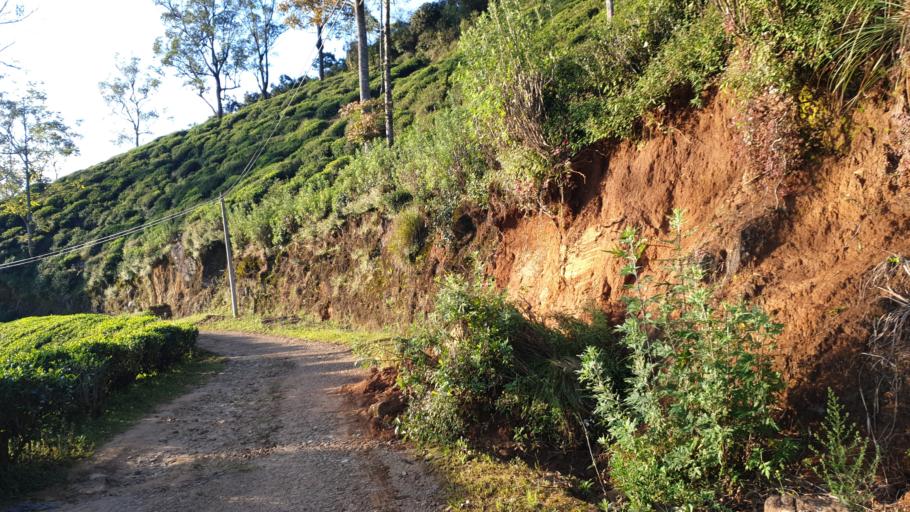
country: LK
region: Central
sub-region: Nuwara Eliya District
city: Nuwara Eliya
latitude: 6.9576
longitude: 80.7638
